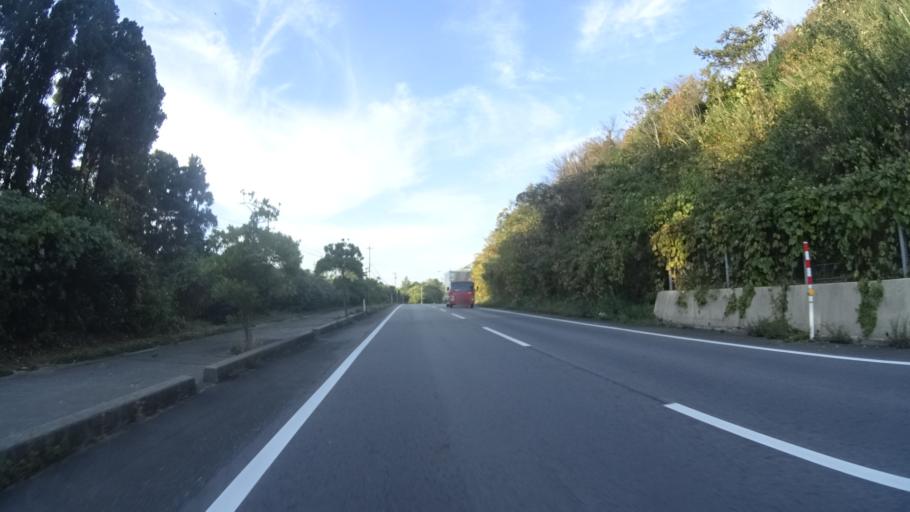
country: JP
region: Ishikawa
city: Hakui
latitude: 37.1118
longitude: 136.7281
